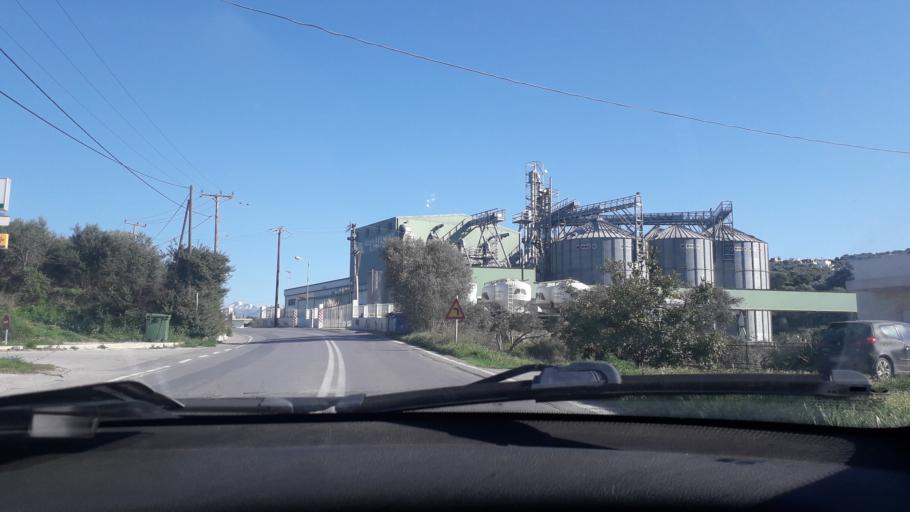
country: GR
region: Crete
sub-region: Nomos Rethymnis
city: Rethymno
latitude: 35.3594
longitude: 24.5498
